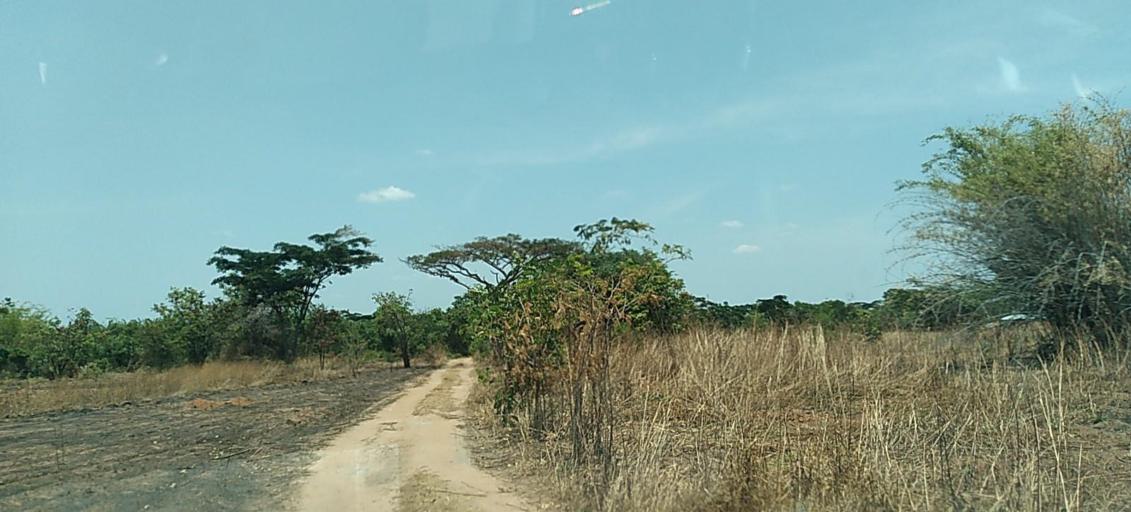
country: ZM
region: Copperbelt
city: Luanshya
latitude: -13.0643
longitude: 28.4063
